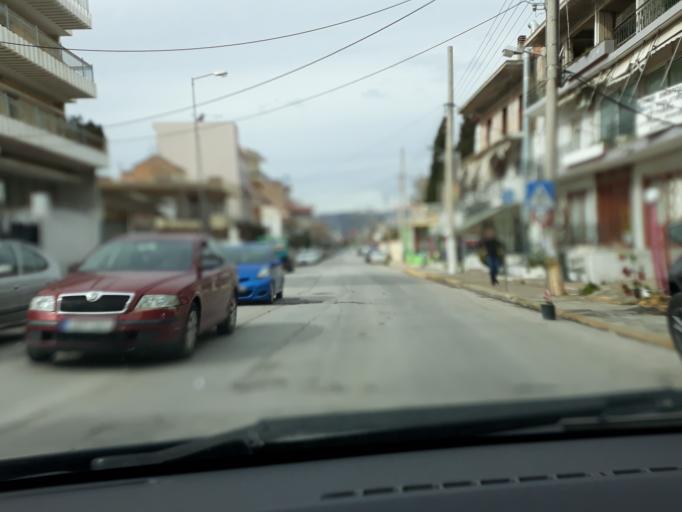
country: GR
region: Attica
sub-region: Nomarchia Anatolikis Attikis
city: Acharnes
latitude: 38.0828
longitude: 23.7324
